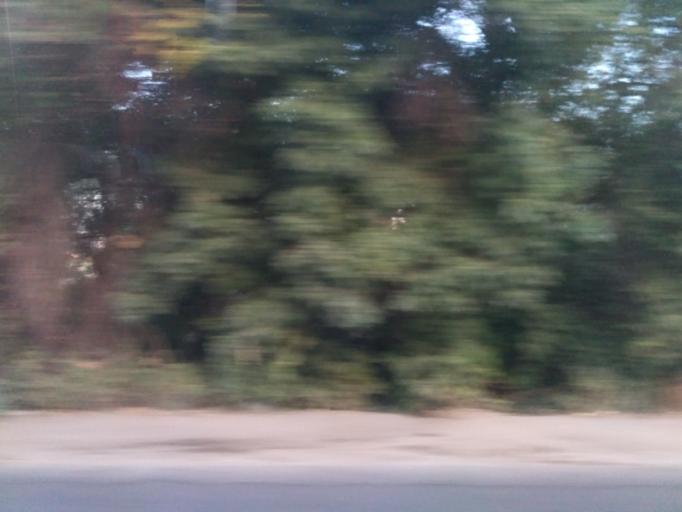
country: KZ
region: Almaty Oblysy
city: Burunday
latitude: 43.3146
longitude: 76.9016
